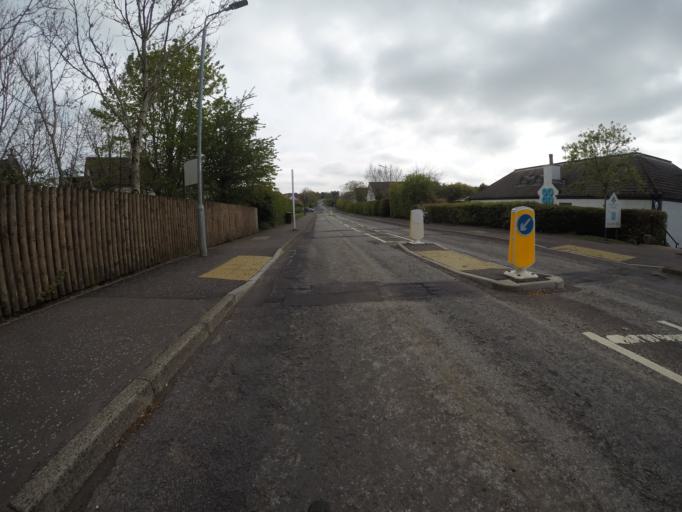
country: GB
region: Scotland
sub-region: East Renfrewshire
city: Busby
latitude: 55.7743
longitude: -4.3047
